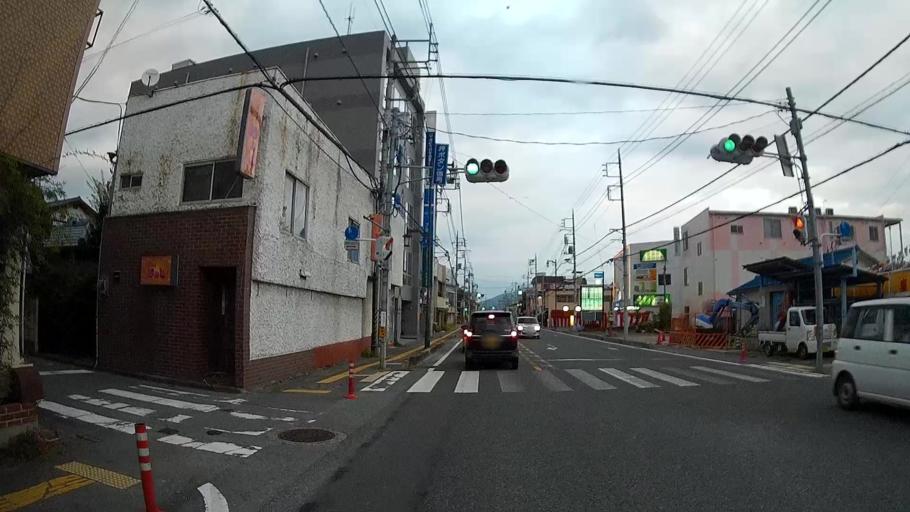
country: JP
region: Saitama
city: Chichibu
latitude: 35.9899
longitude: 139.0856
